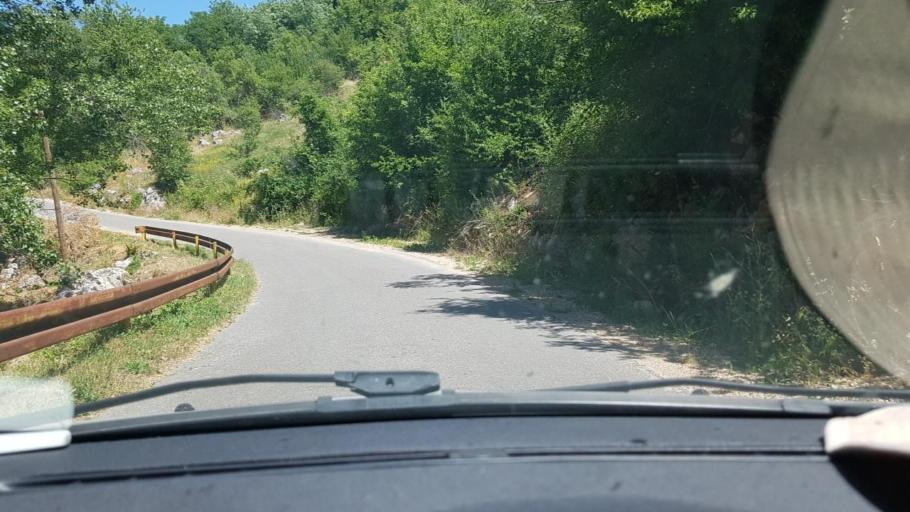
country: HR
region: Licko-Senjska
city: Otocac
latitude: 44.7891
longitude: 15.3686
